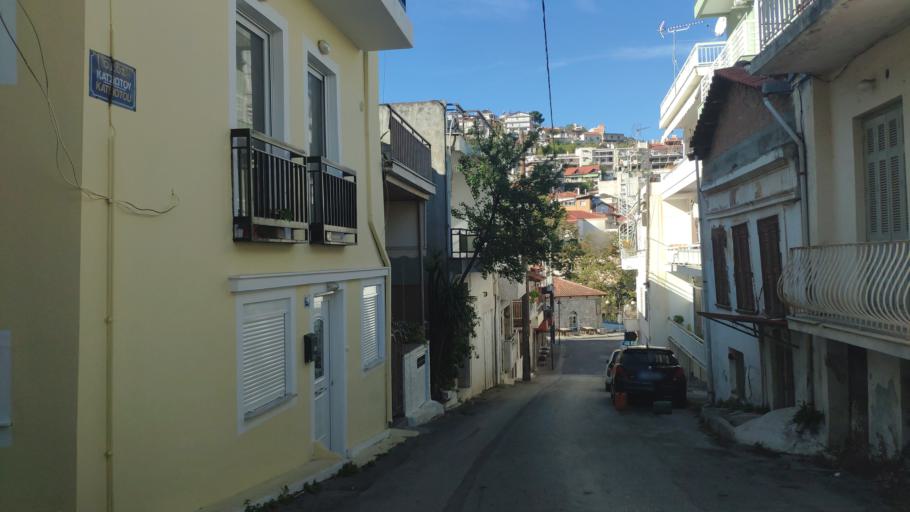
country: GR
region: Central Greece
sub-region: Nomos Voiotias
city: Livadeia
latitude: 38.4337
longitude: 22.8760
